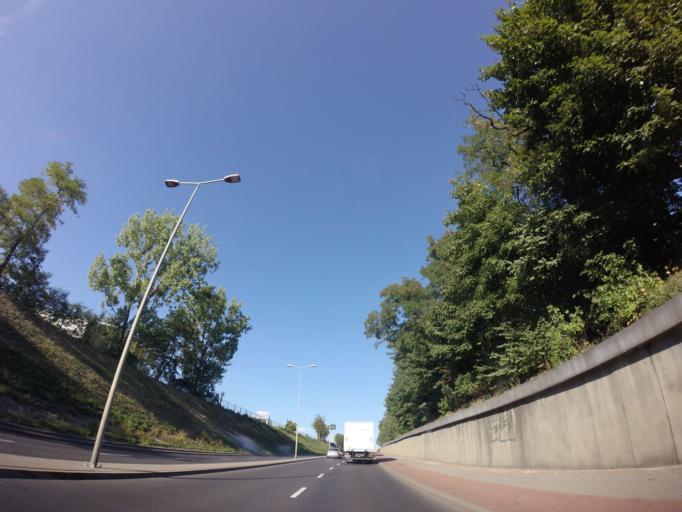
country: PL
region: Lubusz
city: Gorzow Wielkopolski
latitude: 52.7389
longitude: 15.2601
